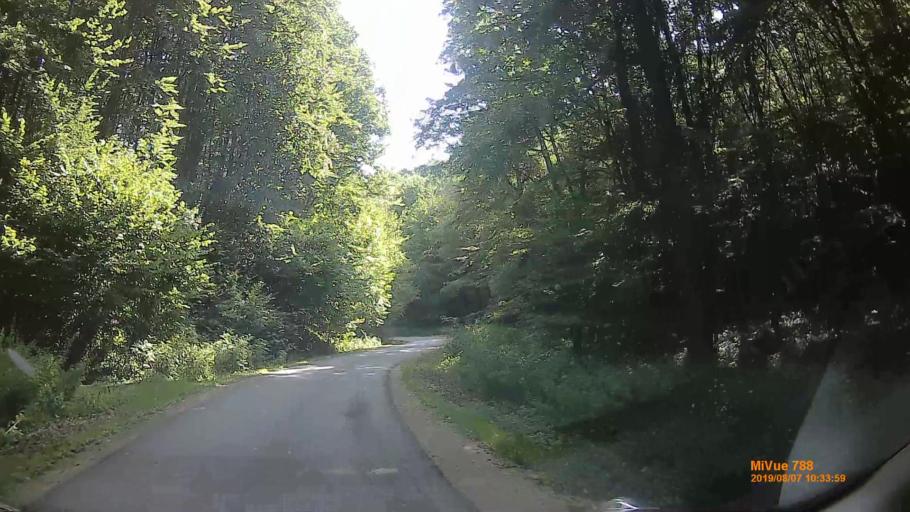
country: HU
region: Veszprem
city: Ajka
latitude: 47.0627
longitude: 17.5951
